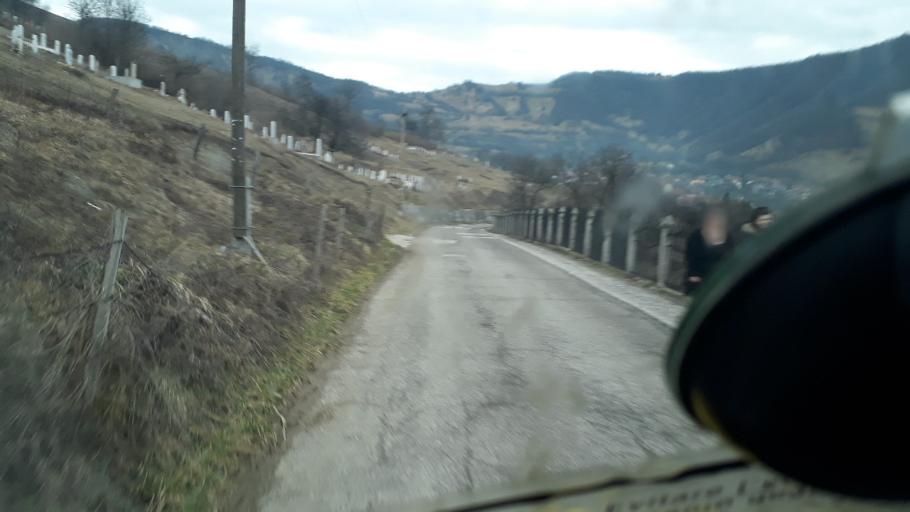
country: BA
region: Federation of Bosnia and Herzegovina
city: Zenica
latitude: 44.1564
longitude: 17.9690
